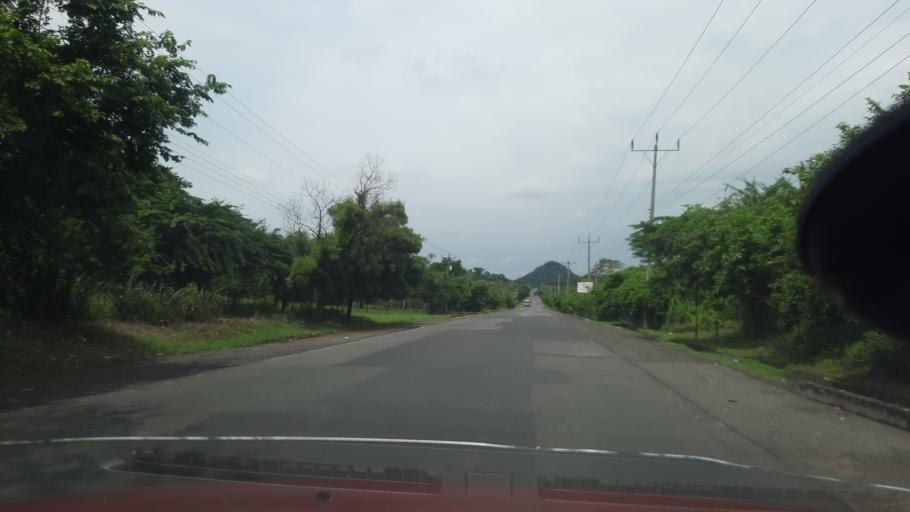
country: SV
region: La Union
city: Pasaquina
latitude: 13.6136
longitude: -87.8525
